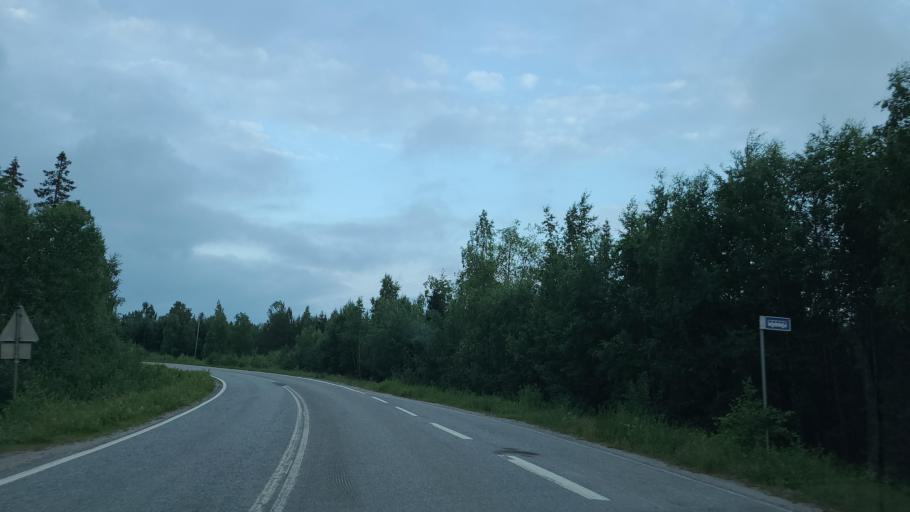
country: FI
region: Ostrobothnia
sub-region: Vaasa
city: Replot
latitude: 63.2923
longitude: 21.1095
